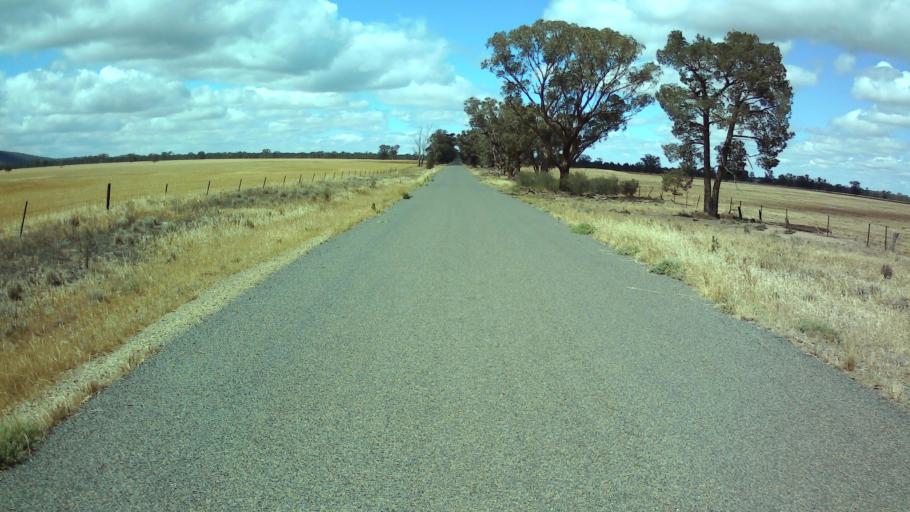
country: AU
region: New South Wales
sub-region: Weddin
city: Grenfell
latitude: -33.8824
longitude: 147.9242
